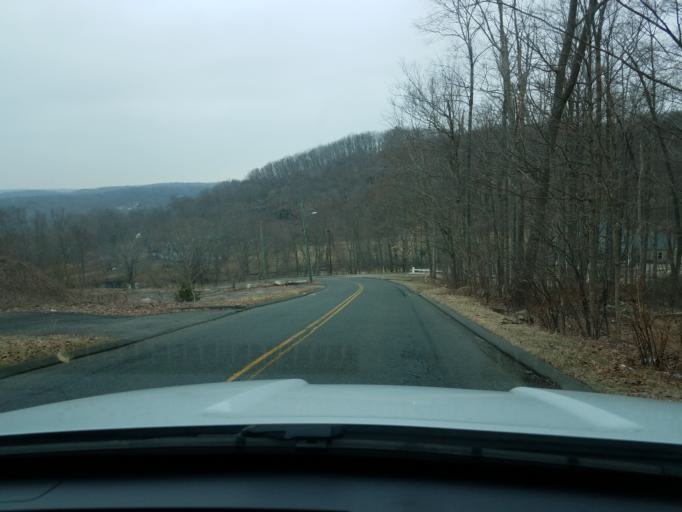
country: US
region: Connecticut
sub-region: New Haven County
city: Naugatuck
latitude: 41.4363
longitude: -73.0296
